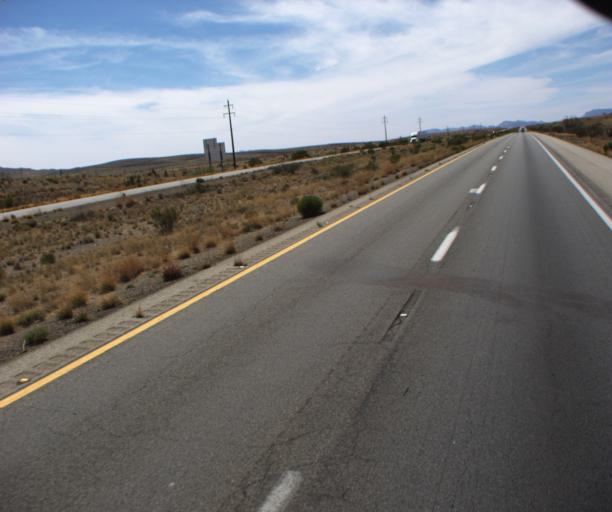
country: US
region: Arizona
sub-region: Cochise County
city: Willcox
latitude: 32.3528
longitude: -109.7204
